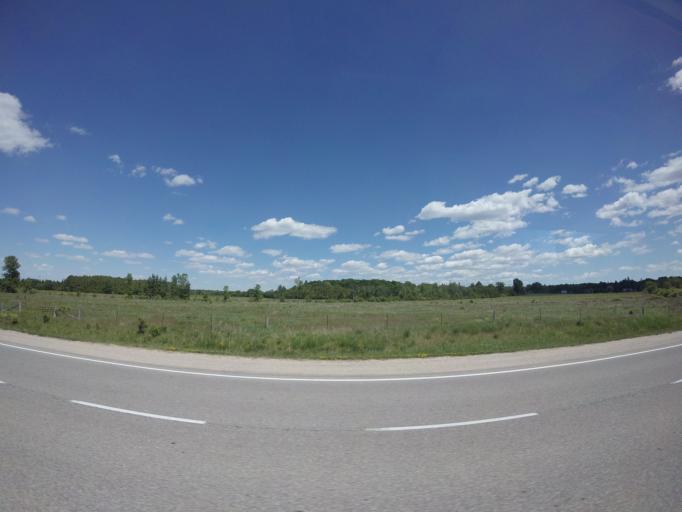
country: CA
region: Ontario
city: Perth
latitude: 44.9894
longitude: -76.2277
